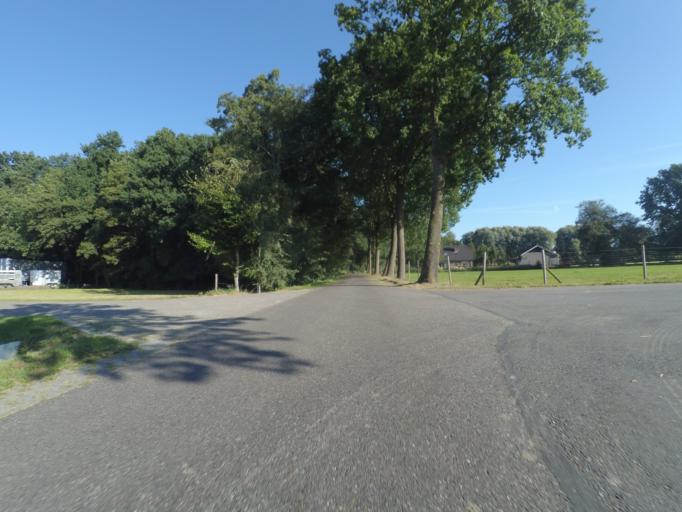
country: NL
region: Gelderland
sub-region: Gemeente Putten
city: Putten
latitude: 52.2528
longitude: 5.5802
